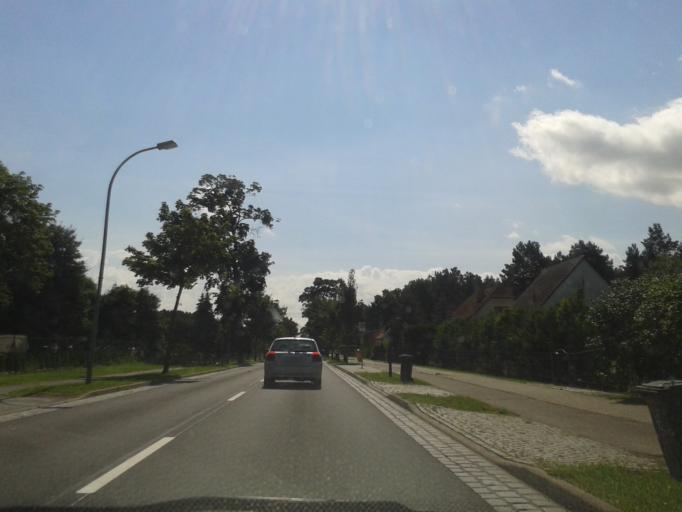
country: DE
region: Mecklenburg-Vorpommern
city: Jatznick
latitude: 53.5699
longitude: 13.9519
